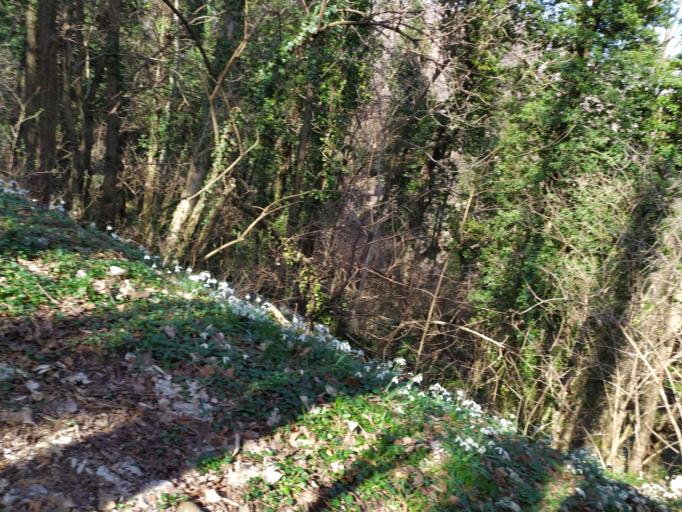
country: IT
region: Veneto
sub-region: Provincia di Vicenza
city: Velo d'Astico
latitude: 45.7903
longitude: 11.3792
